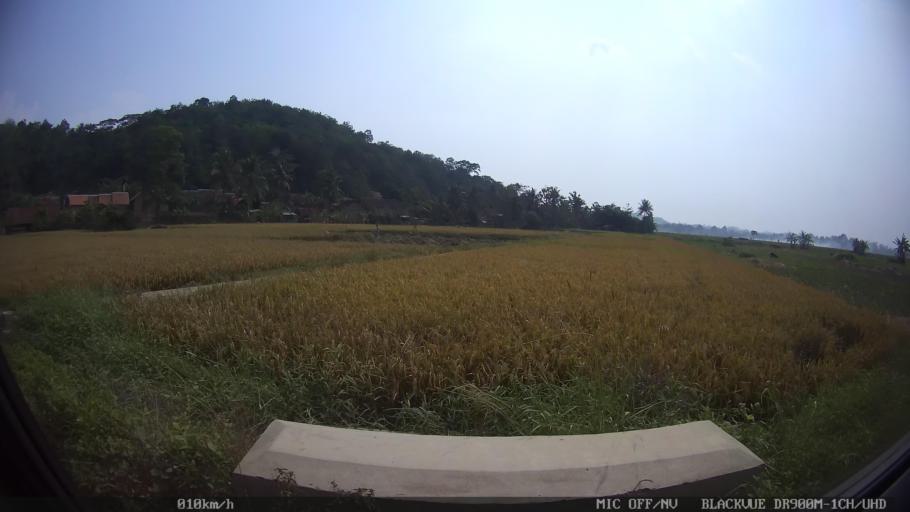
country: ID
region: Lampung
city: Pringsewu
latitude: -5.3748
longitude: 104.9985
